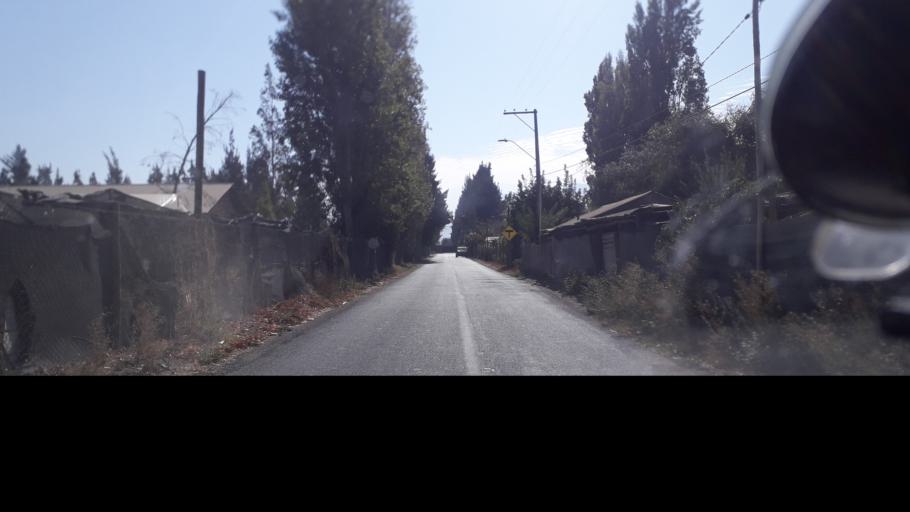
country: CL
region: Valparaiso
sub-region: Provincia de San Felipe
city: Llaillay
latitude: -32.8541
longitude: -70.9423
